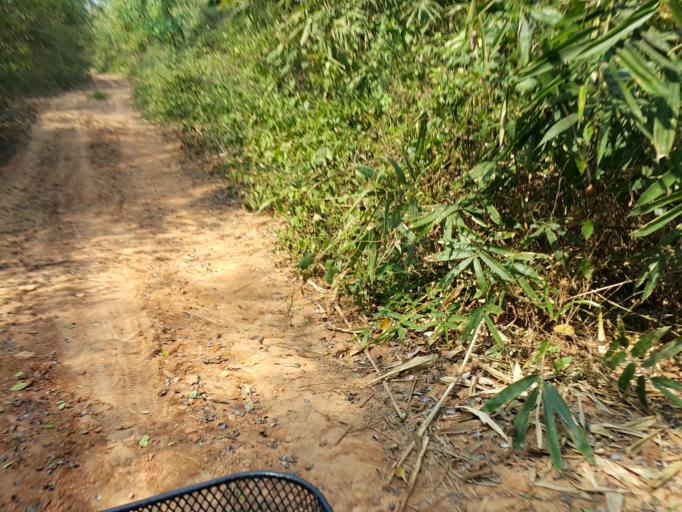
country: TH
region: Sukhothai
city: Thung Saliam
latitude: 17.3259
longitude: 99.4990
